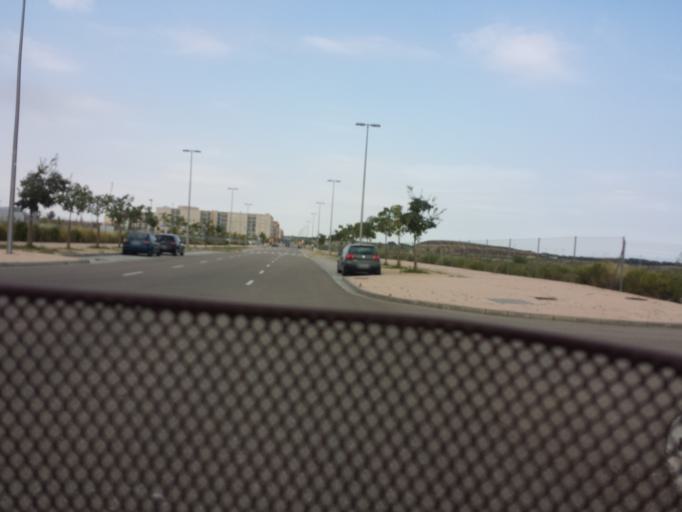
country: ES
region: Aragon
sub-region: Provincia de Zaragoza
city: Montecanal
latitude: 41.6247
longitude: -0.9532
